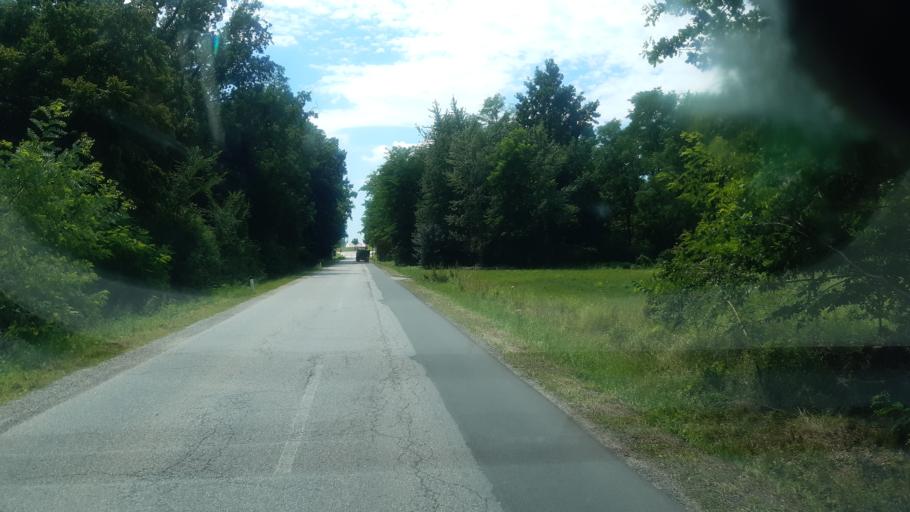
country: SI
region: Beltinci
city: Gancani
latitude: 46.6421
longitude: 16.2641
